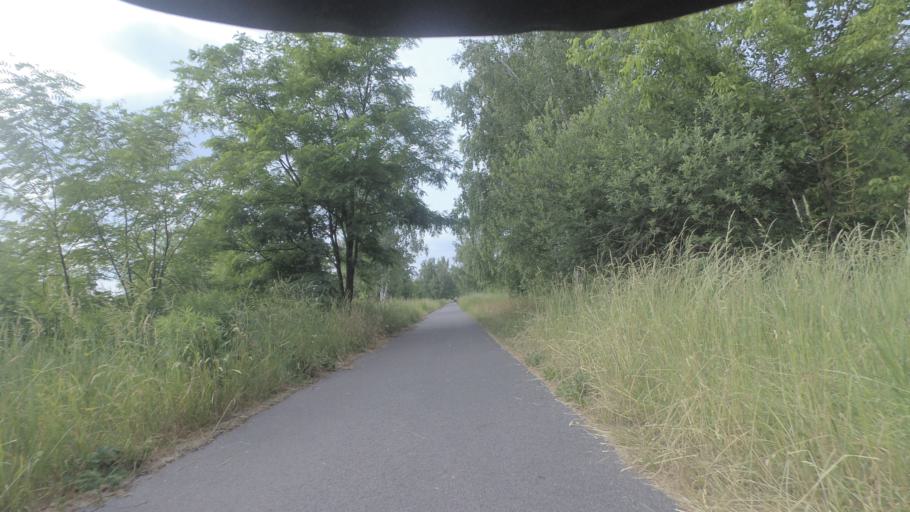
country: DE
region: Berlin
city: Gropiusstadt
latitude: 52.4143
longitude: 13.4698
